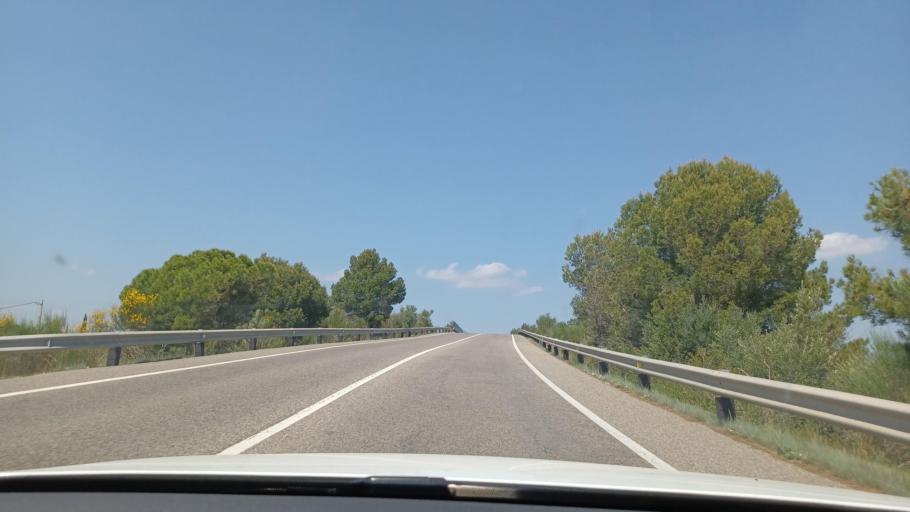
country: ES
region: Catalonia
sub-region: Provincia de Tarragona
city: L'Ampolla
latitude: 40.8009
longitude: 0.6931
